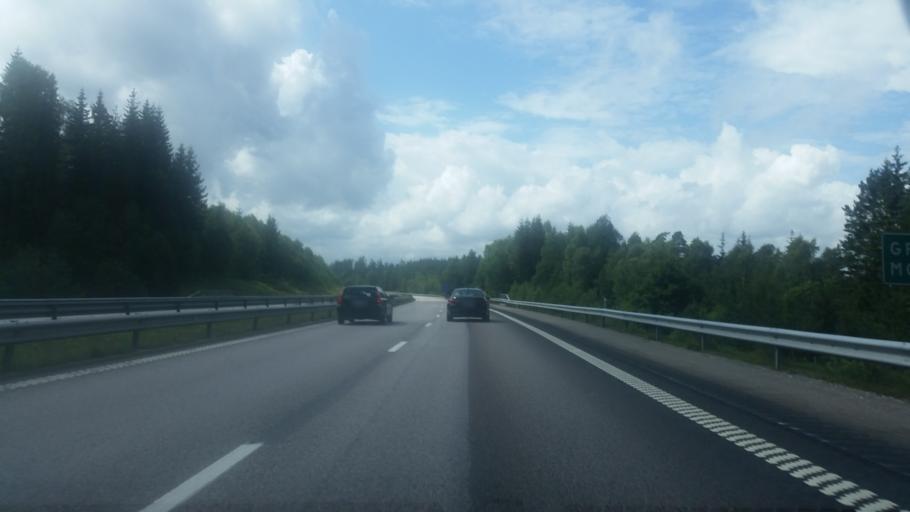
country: SE
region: Vaestra Goetaland
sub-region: Bollebygds Kommun
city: Bollebygd
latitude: 57.6710
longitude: 12.6241
